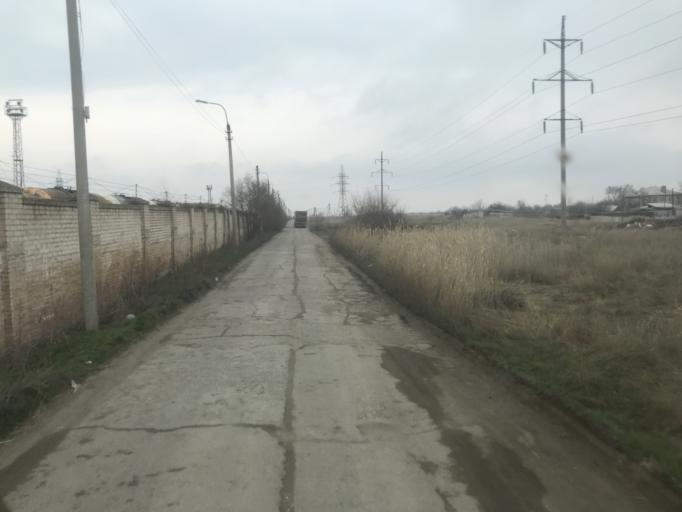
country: RU
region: Volgograd
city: Krasnoslobodsk
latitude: 48.5308
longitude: 44.5881
